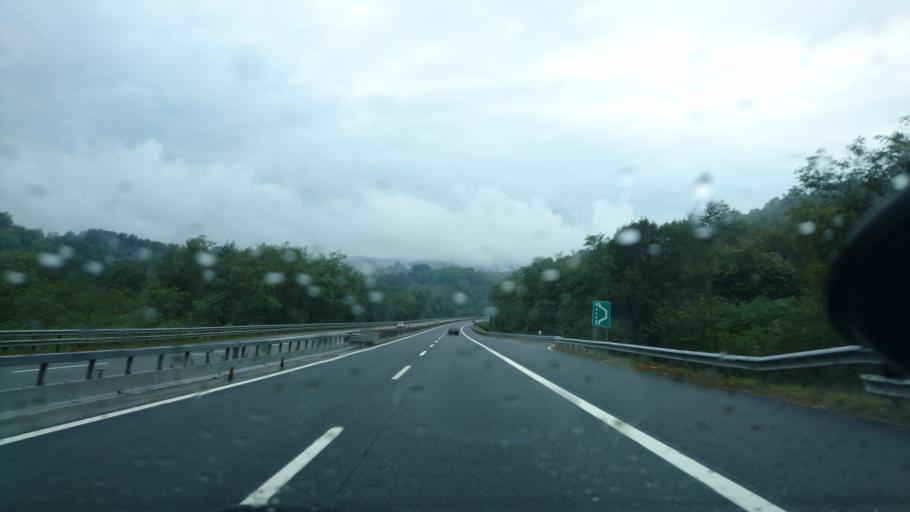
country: IT
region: Piedmont
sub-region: Provincia di Novara
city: Invorio
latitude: 45.7609
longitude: 8.4992
